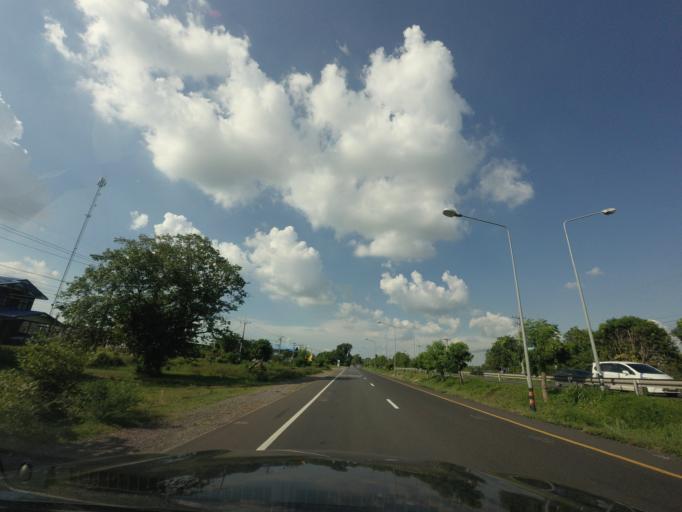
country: TH
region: Nakhon Ratchasima
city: Bua Lai
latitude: 15.6809
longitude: 102.5770
